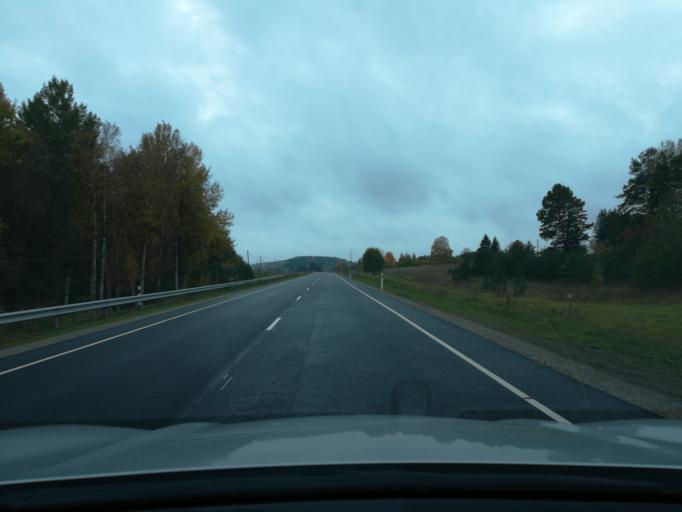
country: EE
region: Ida-Virumaa
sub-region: Johvi vald
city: Johvi
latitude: 59.1274
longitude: 27.3281
